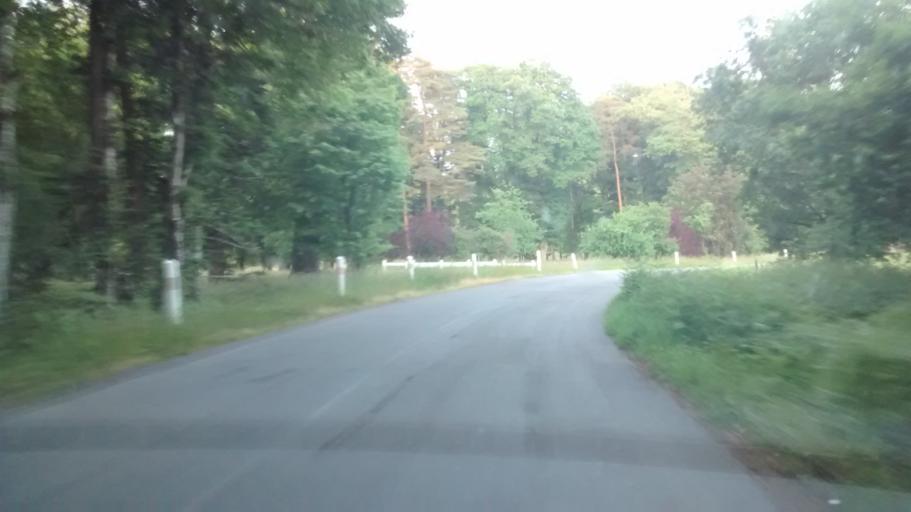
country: FR
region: Brittany
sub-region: Departement d'Ille-et-Vilaine
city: Paimpont
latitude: 47.9968
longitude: -2.1455
